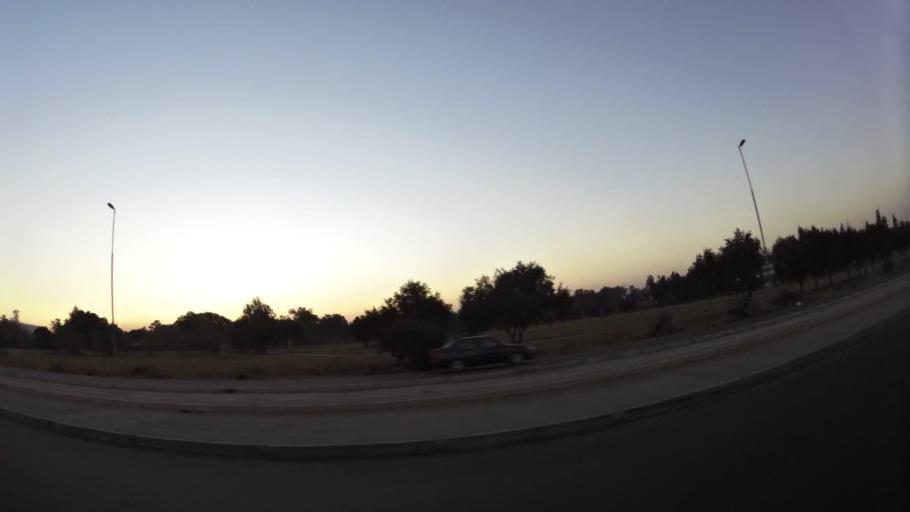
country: ZA
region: North-West
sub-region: Bojanala Platinum District Municipality
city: Rustenburg
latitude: -25.6436
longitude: 27.2607
